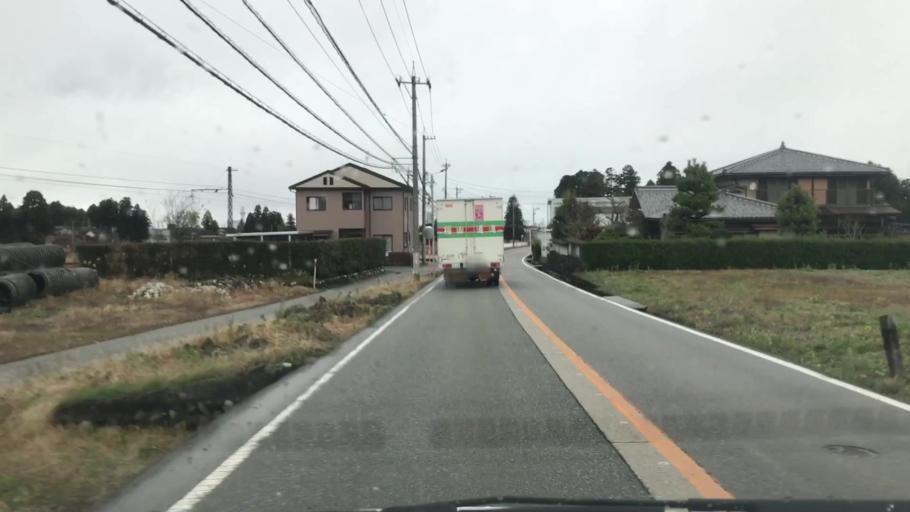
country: JP
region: Toyama
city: Kamiichi
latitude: 36.6020
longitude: 137.3215
